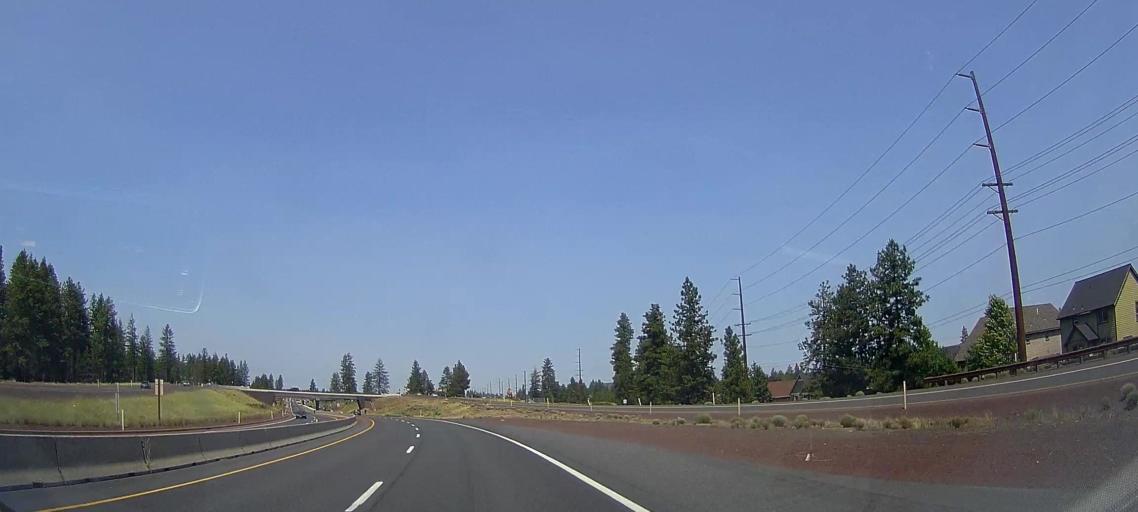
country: US
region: Oregon
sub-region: Deschutes County
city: Bend
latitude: 44.0145
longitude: -121.3194
